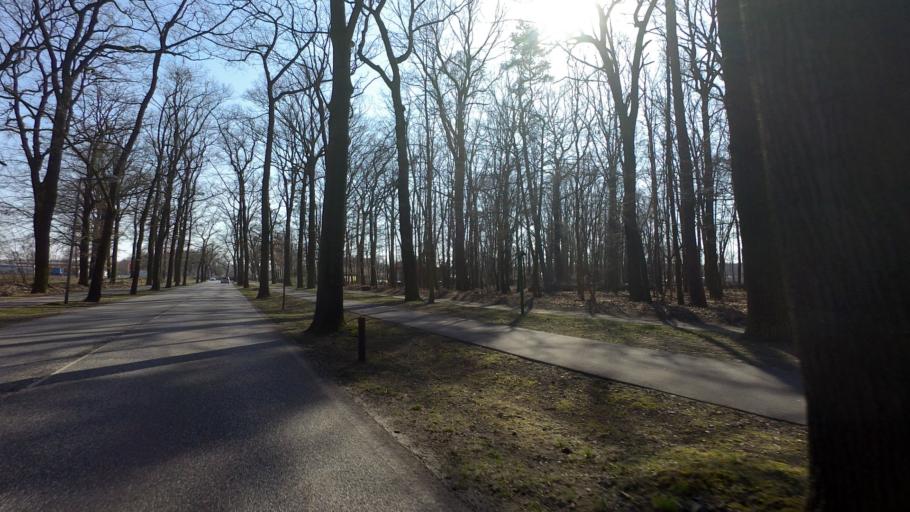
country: DE
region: Brandenburg
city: Hennigsdorf
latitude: 52.6239
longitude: 13.2035
